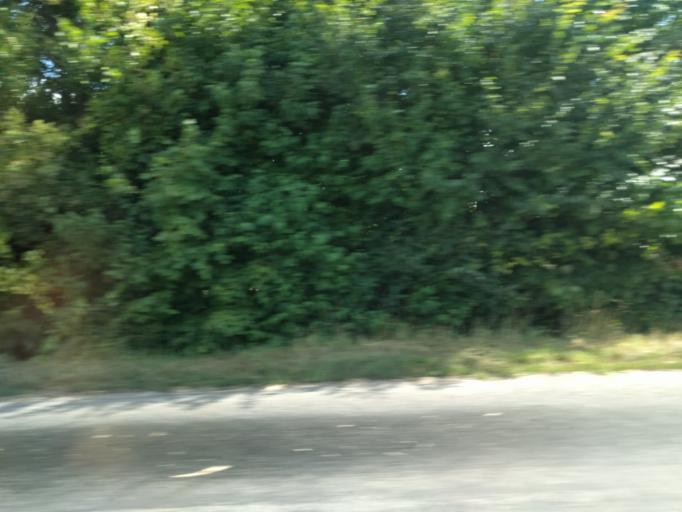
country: DK
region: Zealand
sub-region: Vordingborg Kommune
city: Stege
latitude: 54.9608
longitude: 12.2659
